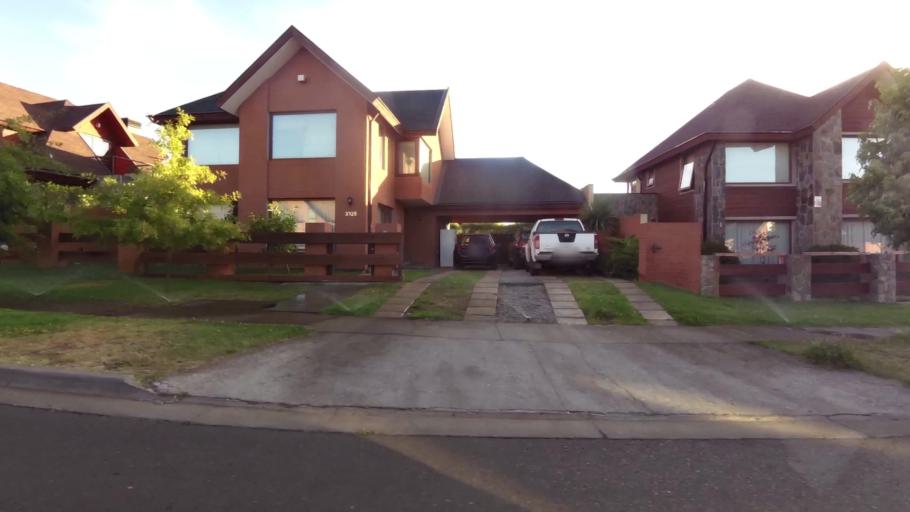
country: CL
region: Biobio
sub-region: Provincia de Concepcion
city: Concepcion
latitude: -36.8587
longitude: -73.1018
